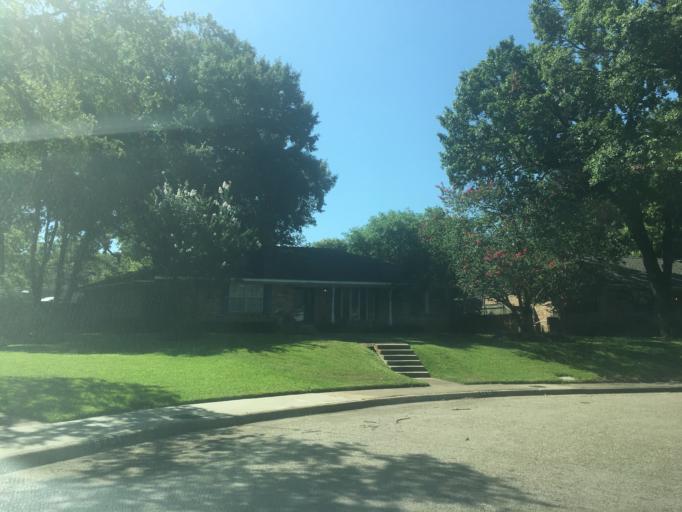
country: US
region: Texas
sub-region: Dallas County
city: Richardson
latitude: 32.8750
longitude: -96.7217
